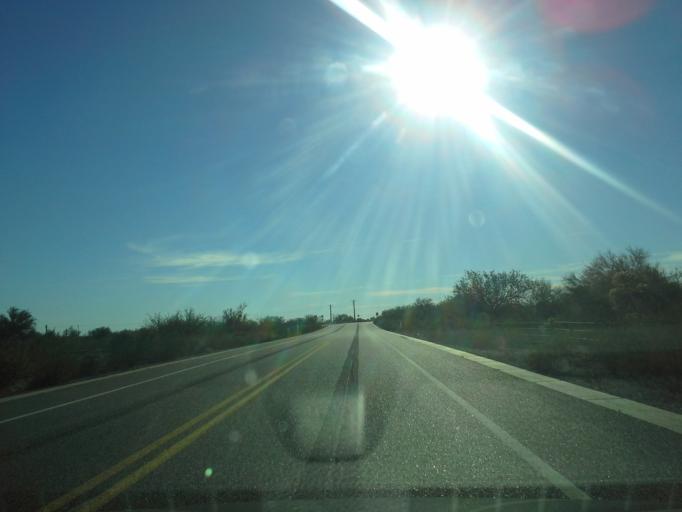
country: US
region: Arizona
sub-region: Pinal County
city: Gold Camp
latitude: 33.2966
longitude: -111.3846
